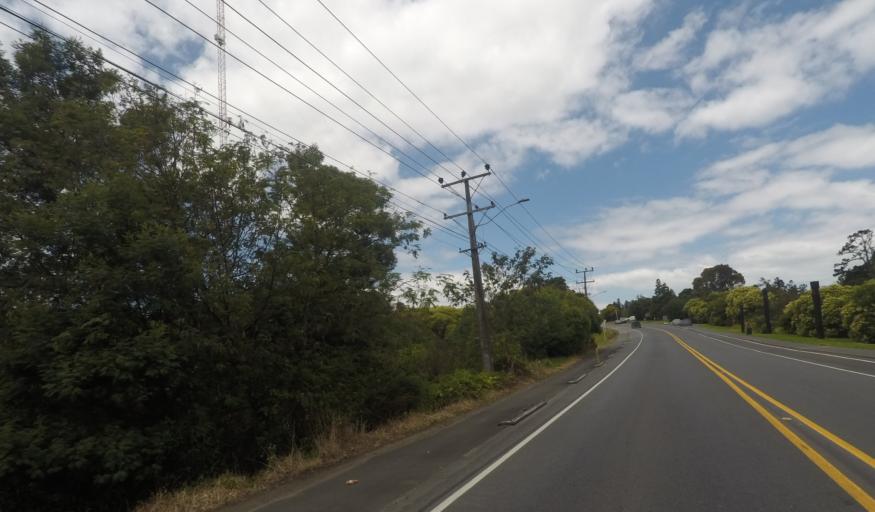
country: NZ
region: Auckland
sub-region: Auckland
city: Rosebank
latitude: -36.8486
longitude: 174.6278
